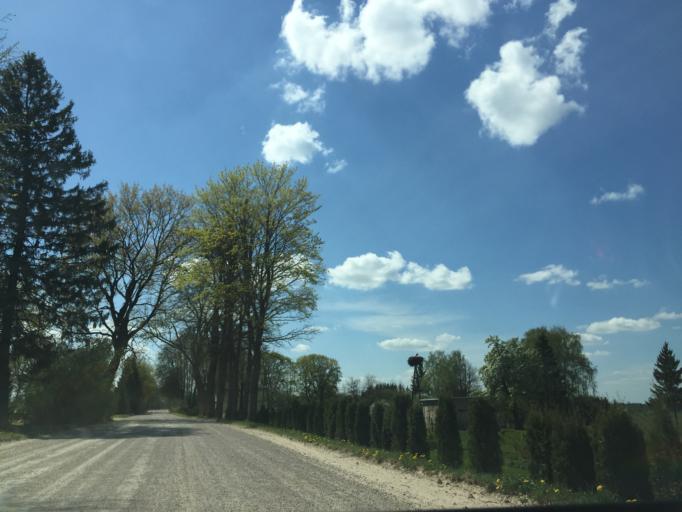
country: LV
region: Vecumnieki
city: Vecumnieki
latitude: 56.4622
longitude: 24.6177
